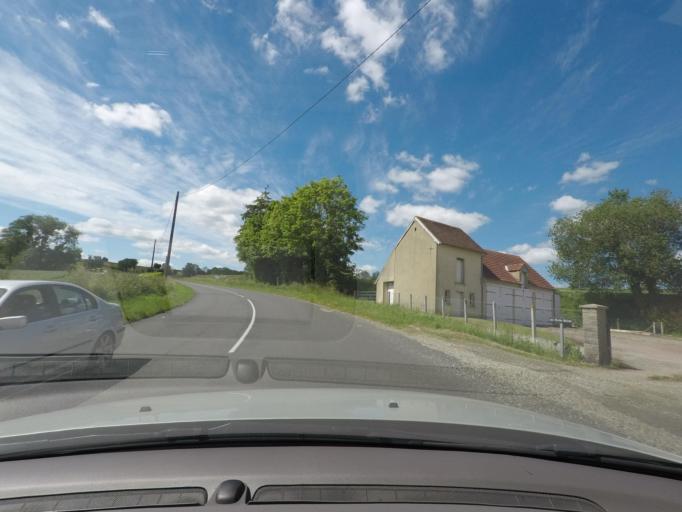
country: FR
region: Lower Normandy
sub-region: Departement de l'Orne
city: Mortagne-au-Perche
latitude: 48.5382
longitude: 0.5596
